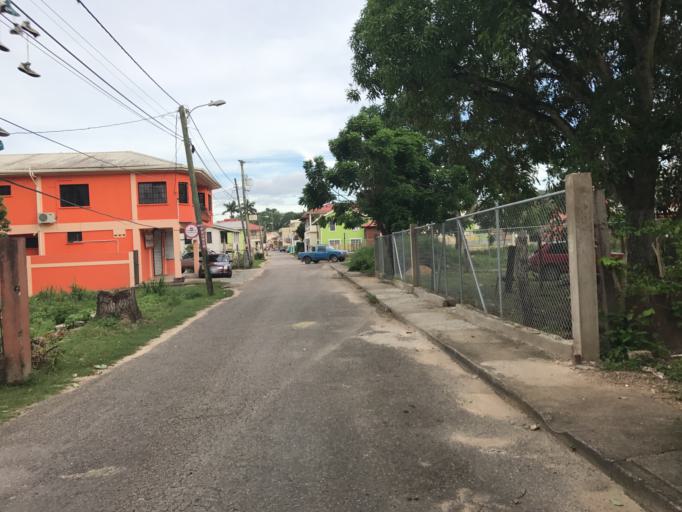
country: BZ
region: Cayo
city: San Ignacio
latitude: 17.1611
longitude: -89.0711
